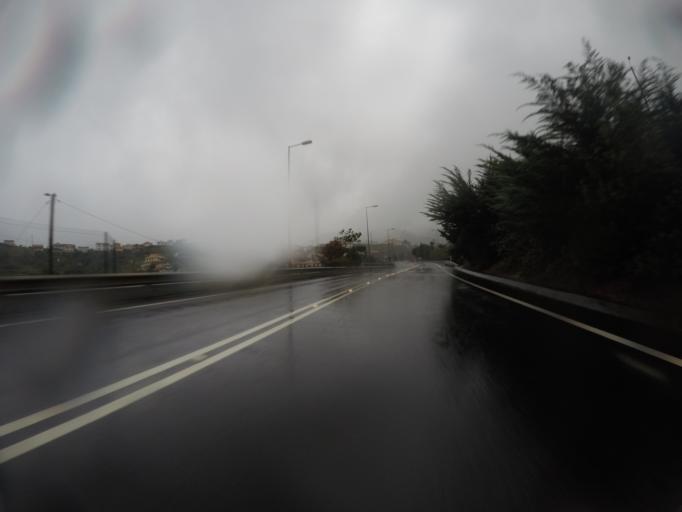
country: PT
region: Madeira
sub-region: Santana
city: Santana
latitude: 32.7627
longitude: -16.8309
